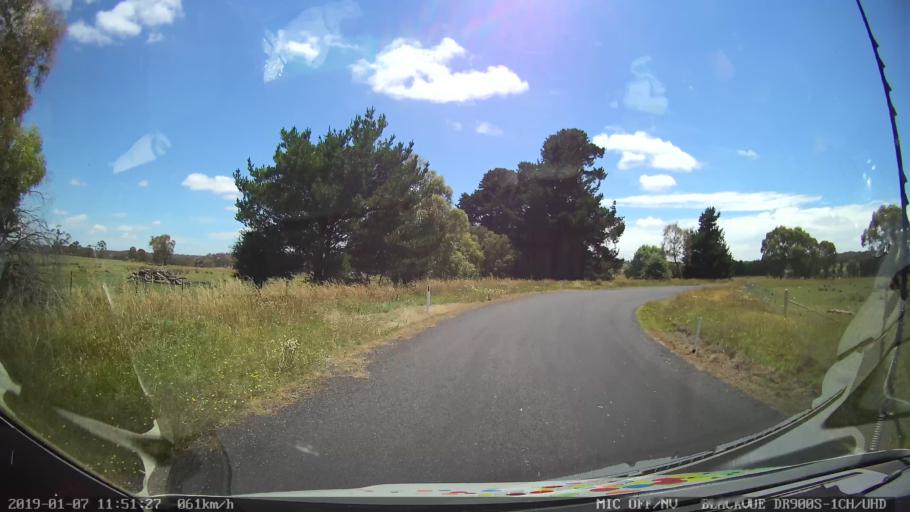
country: AU
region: New South Wales
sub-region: Guyra
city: Guyra
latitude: -30.3079
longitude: 151.6454
